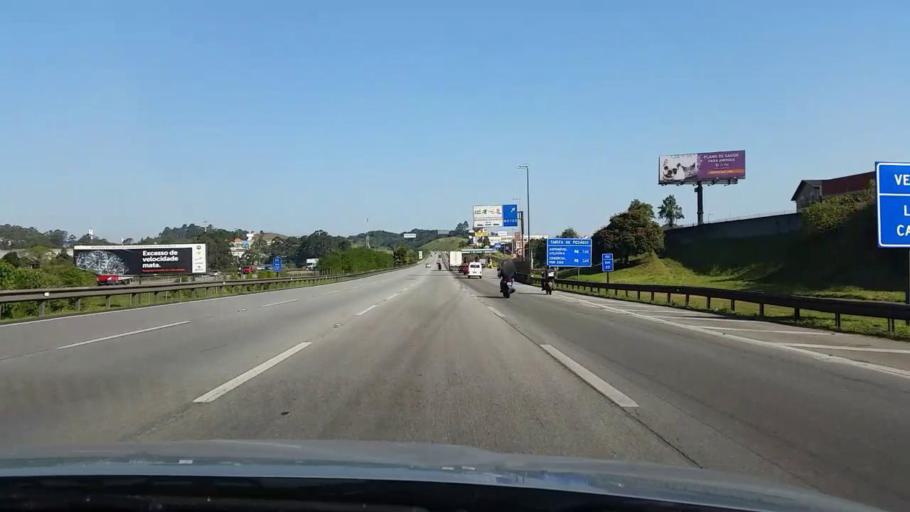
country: BR
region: Sao Paulo
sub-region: Diadema
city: Diadema
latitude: -23.7156
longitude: -46.6052
